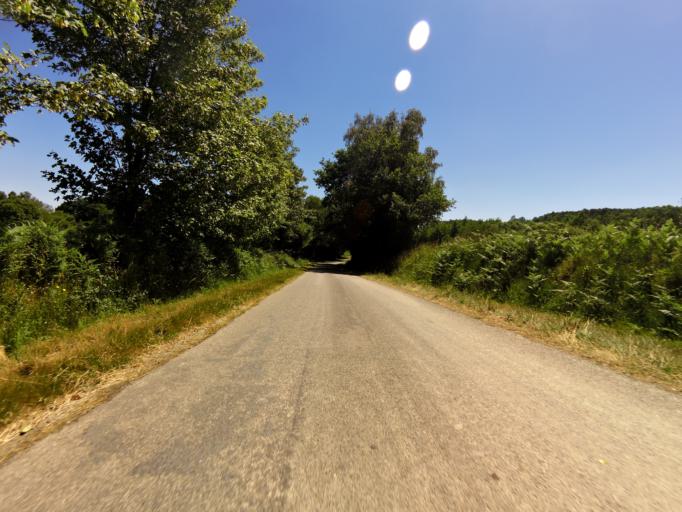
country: FR
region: Brittany
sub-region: Departement du Morbihan
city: Molac
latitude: 47.7105
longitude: -2.4058
